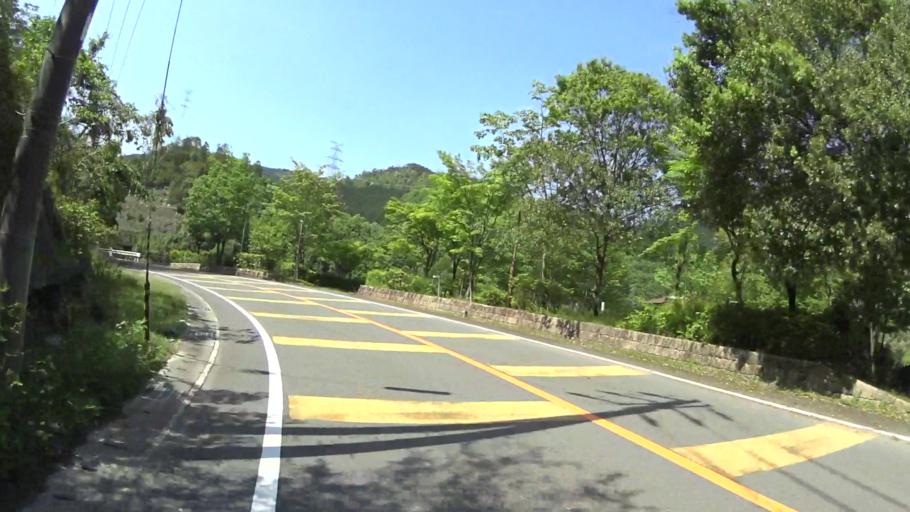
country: JP
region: Kyoto
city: Kameoka
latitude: 35.1286
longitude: 135.5583
